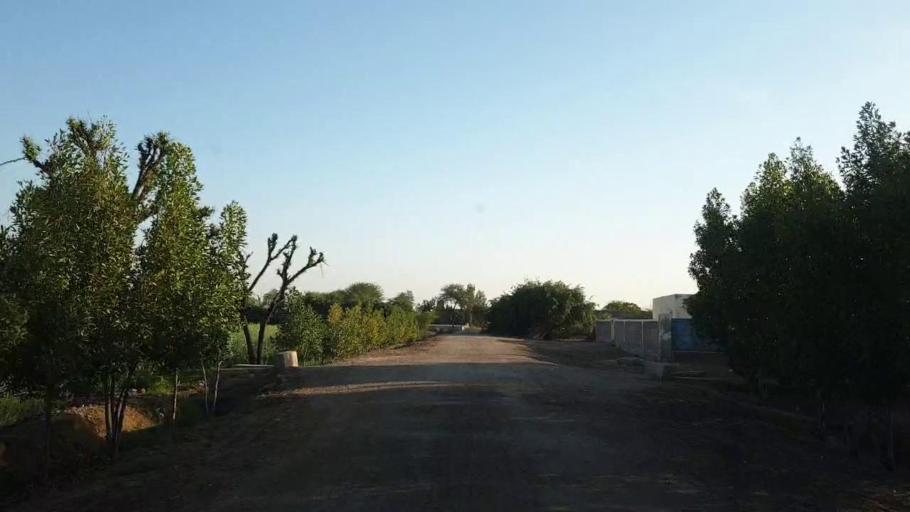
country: PK
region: Sindh
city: Kunri
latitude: 25.0909
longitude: 69.4323
